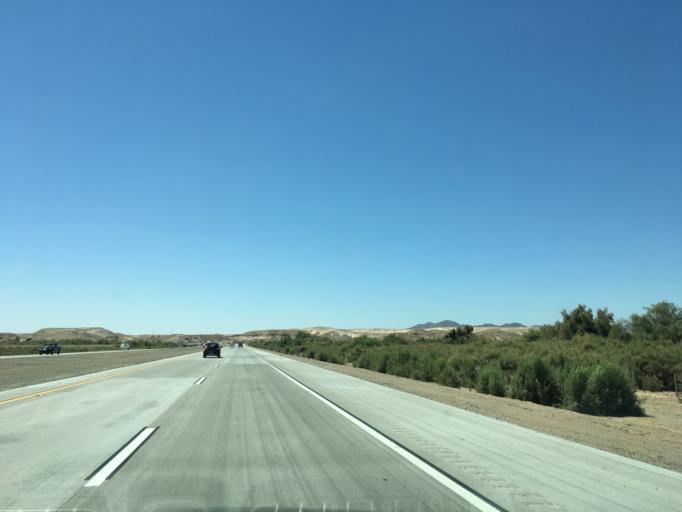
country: MX
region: Baja California
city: Los Algodones
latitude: 32.7430
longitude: -114.6877
